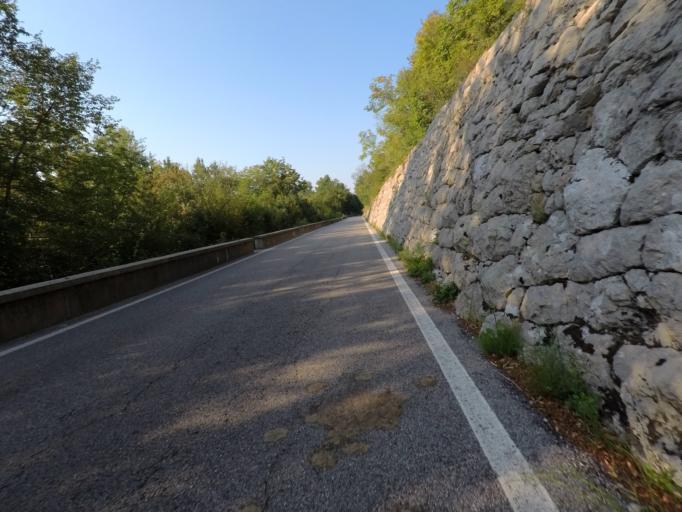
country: IT
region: Friuli Venezia Giulia
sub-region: Provincia di Udine
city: Osoppo
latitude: 46.2374
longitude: 13.0312
